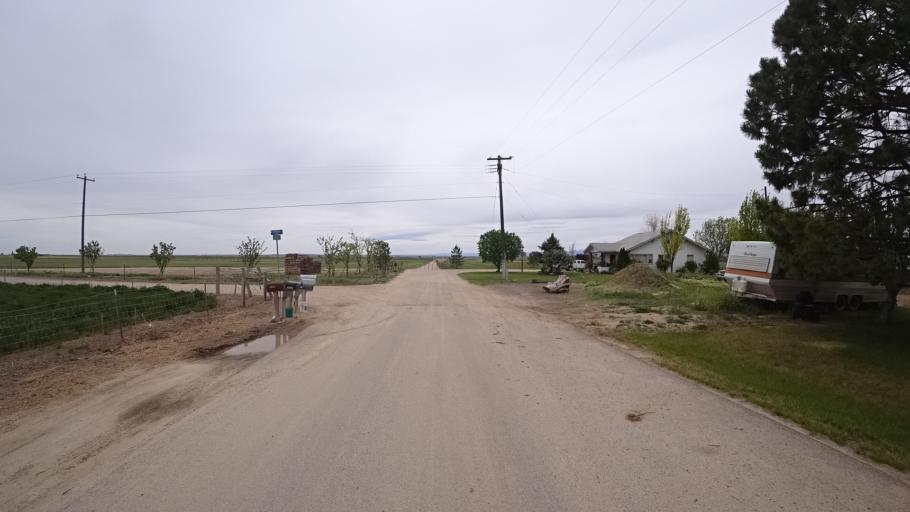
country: US
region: Idaho
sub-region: Ada County
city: Kuna
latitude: 43.4812
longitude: -116.3143
